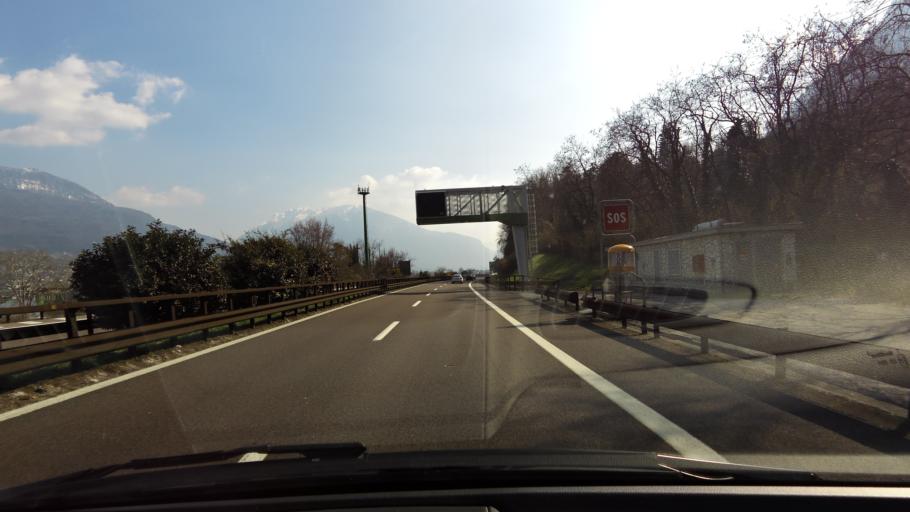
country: IT
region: Trentino-Alto Adige
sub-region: Provincia di Trento
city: Trento
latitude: 46.0647
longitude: 11.1099
